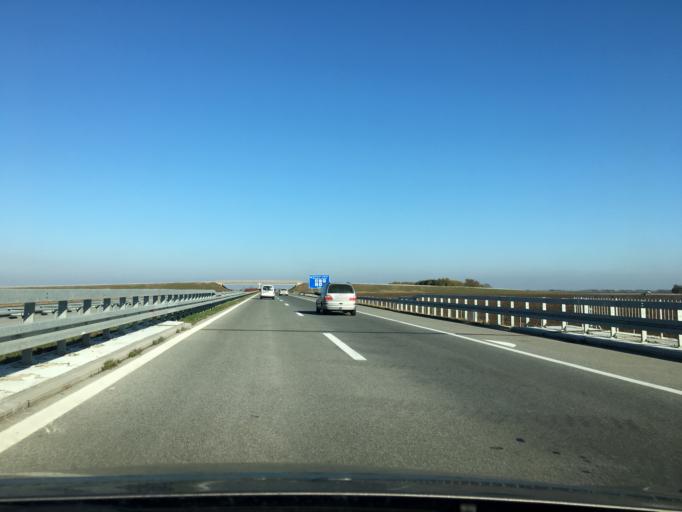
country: RS
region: Autonomna Pokrajina Vojvodina
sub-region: Severnobacki Okrug
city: Mali Igos
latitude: 45.7449
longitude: 19.7027
